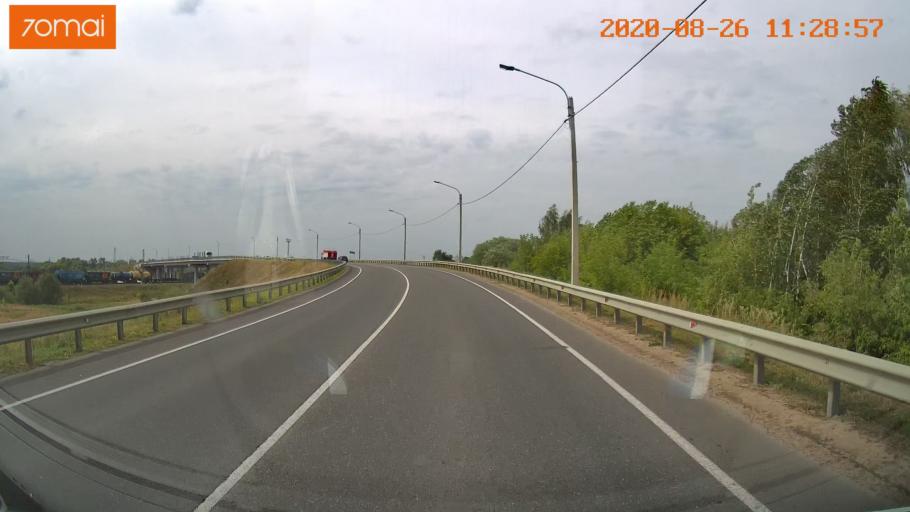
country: RU
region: Rjazan
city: Shilovo
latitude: 54.3233
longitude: 40.9040
